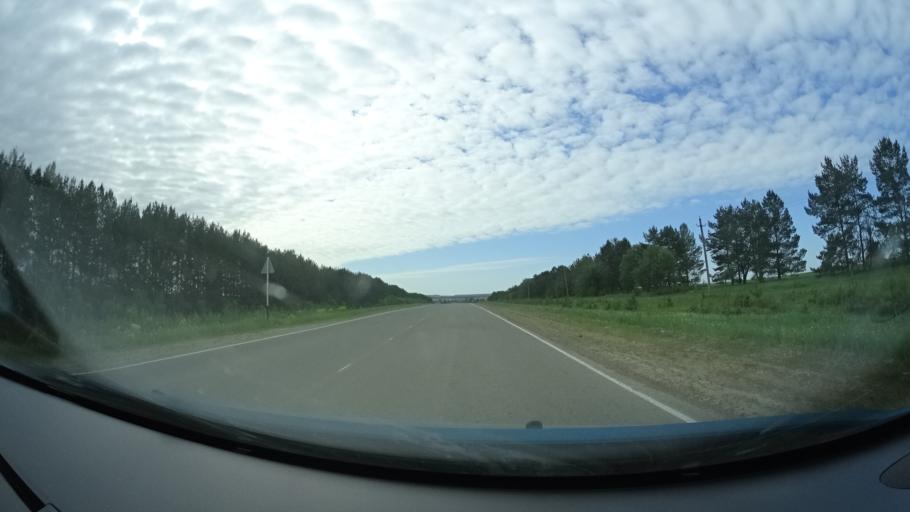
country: RU
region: Perm
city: Kuyeda
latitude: 56.4696
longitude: 55.5888
